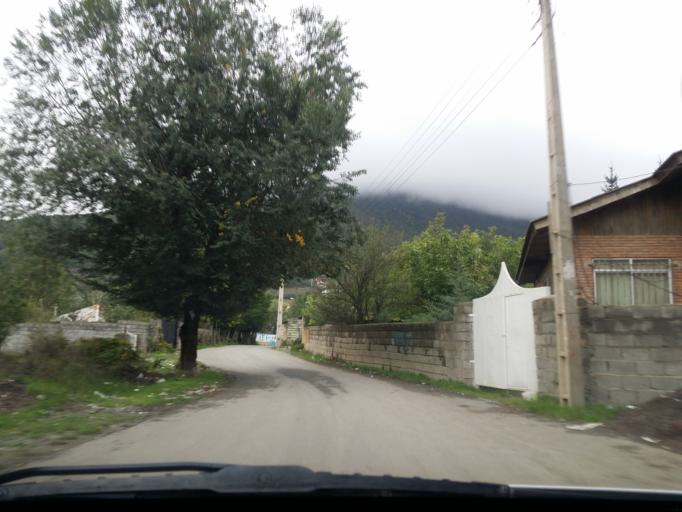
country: IR
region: Mazandaran
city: `Abbasabad
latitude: 36.5079
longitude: 51.1936
